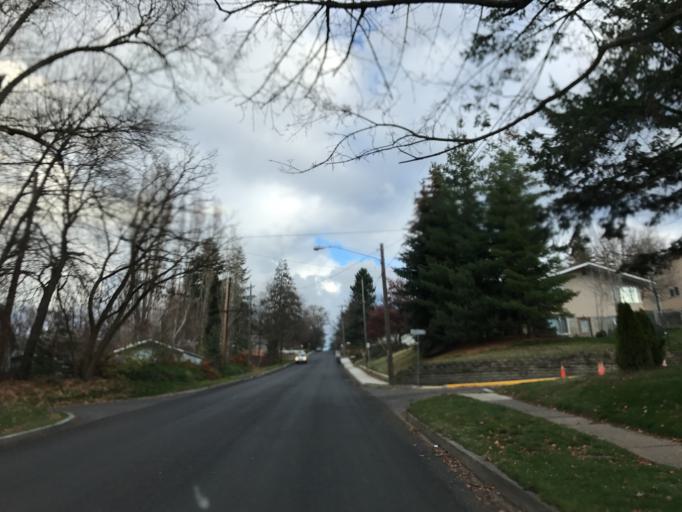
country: US
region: Idaho
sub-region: Latah County
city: Moscow
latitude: 46.7374
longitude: -116.9975
